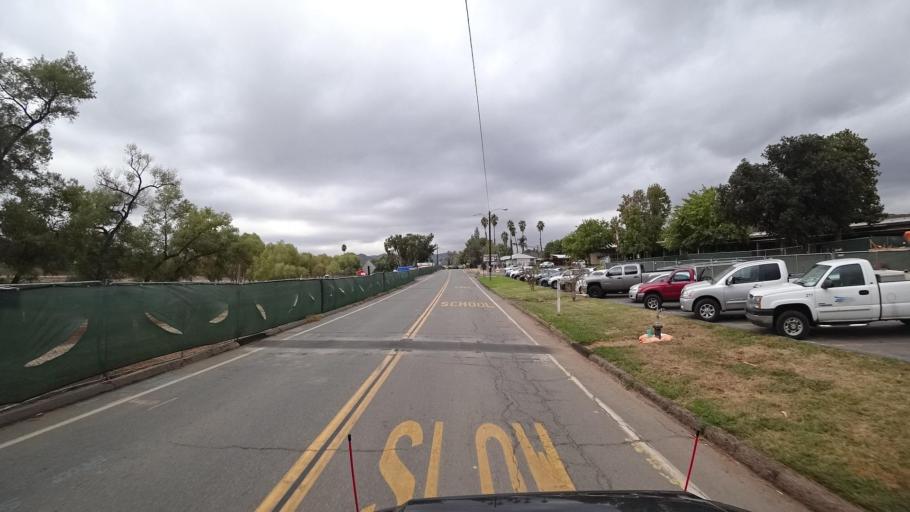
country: US
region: California
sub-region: San Diego County
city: Lakeside
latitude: 32.8588
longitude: -116.9141
